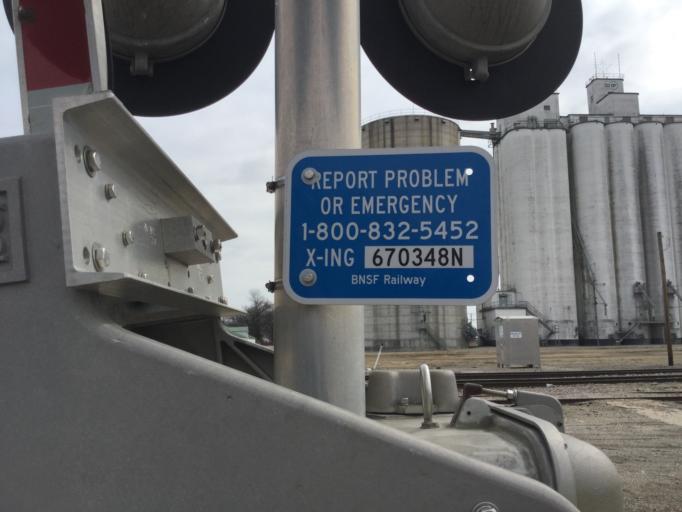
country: US
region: Kansas
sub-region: Cherokee County
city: Columbus
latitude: 37.1718
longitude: -94.8384
